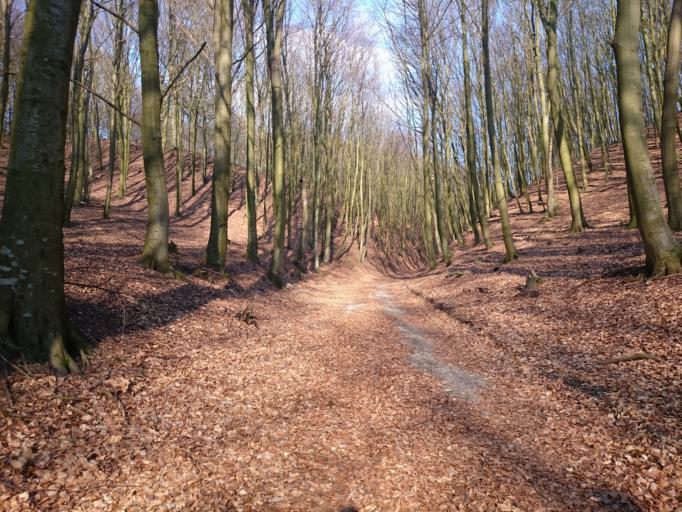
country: SE
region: Skane
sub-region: Sjobo Kommun
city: Sjoebo
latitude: 55.6014
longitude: 13.7615
